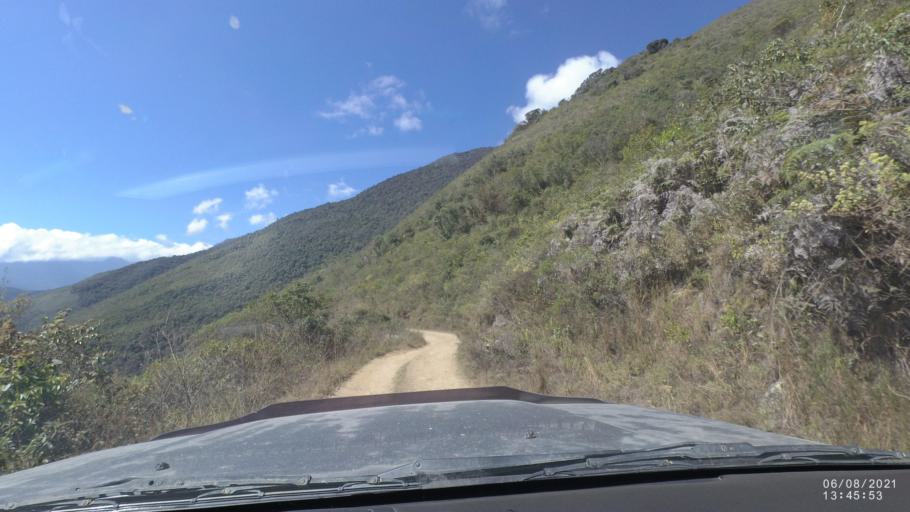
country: BO
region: La Paz
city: Quime
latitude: -16.6706
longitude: -66.7303
